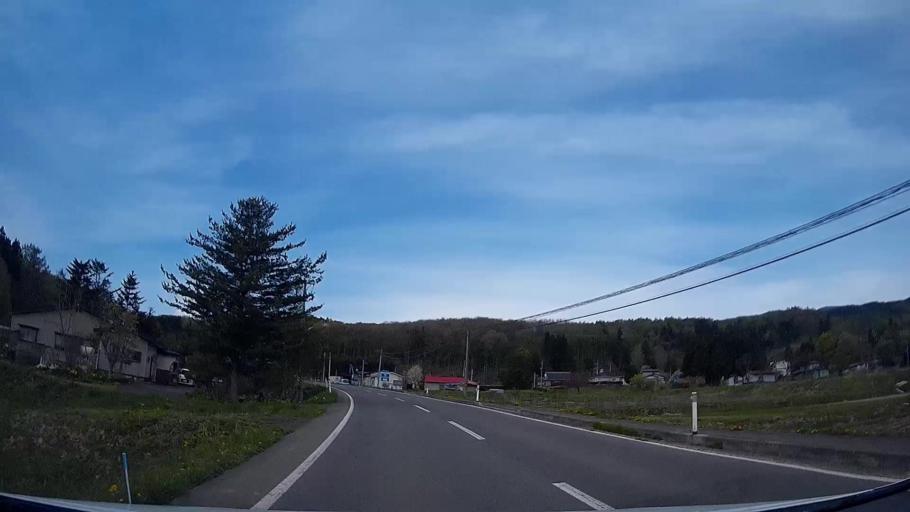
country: JP
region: Iwate
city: Shizukuishi
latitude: 39.9304
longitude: 140.9887
